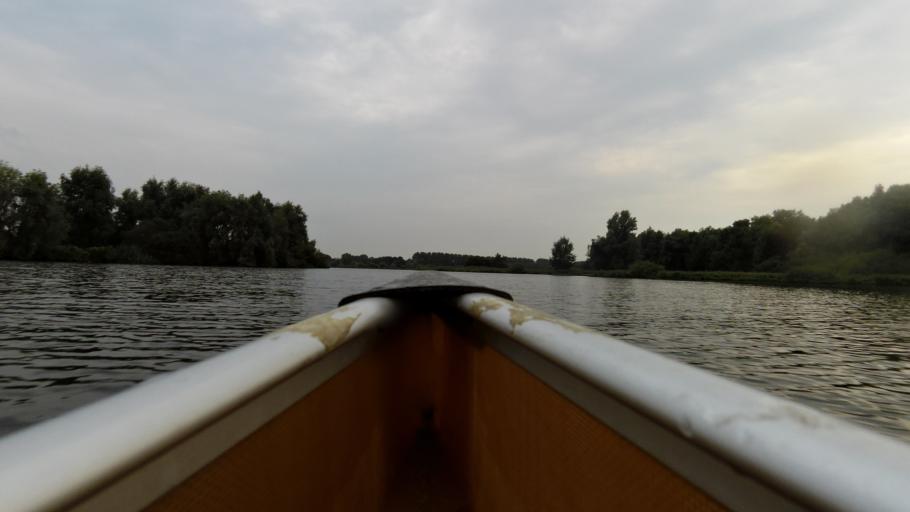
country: NL
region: South Holland
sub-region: Gemeente Leiderdorp
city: Leiderdorp
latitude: 52.1884
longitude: 4.5155
